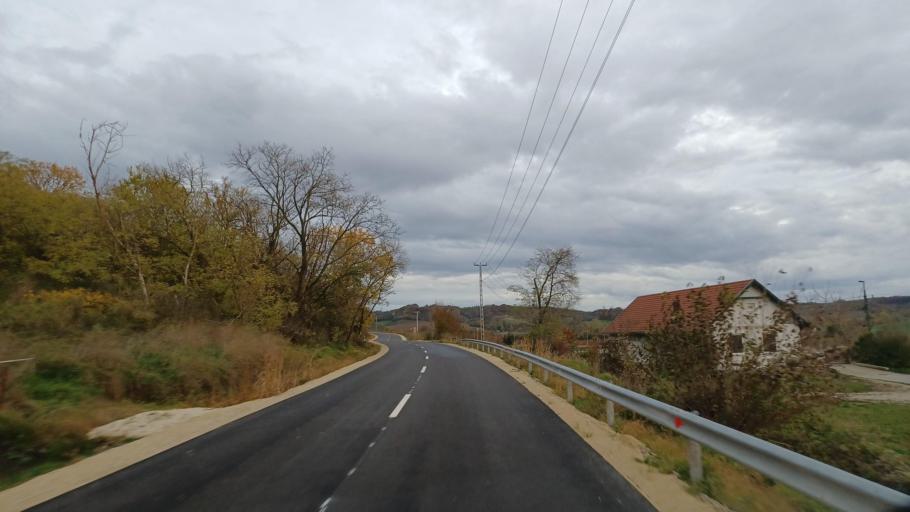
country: HU
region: Tolna
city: Gyonk
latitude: 46.5940
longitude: 18.4297
